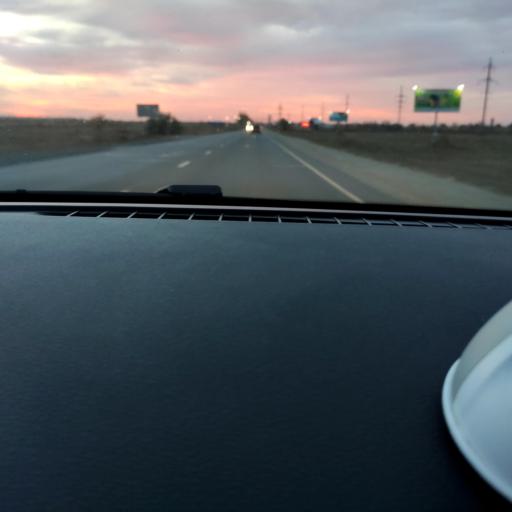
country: RU
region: Samara
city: Samara
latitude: 53.1277
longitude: 50.1645
